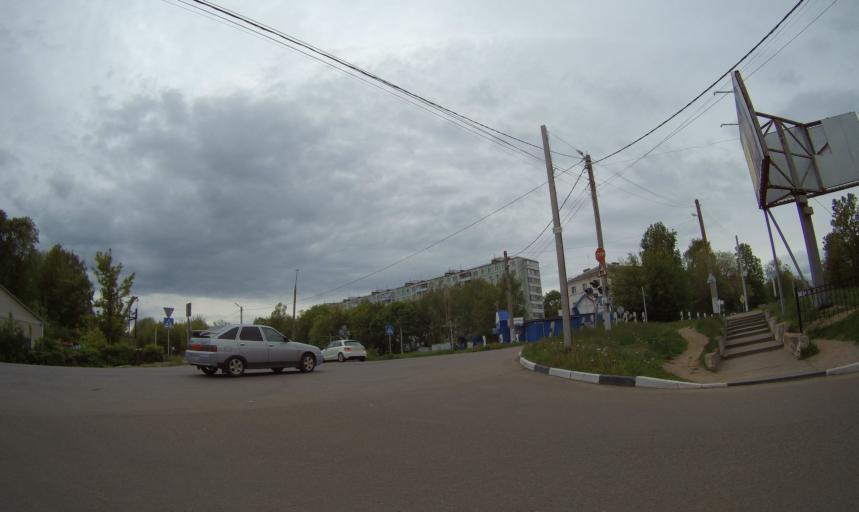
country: RU
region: Moskovskaya
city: Kolomna
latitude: 55.0744
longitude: 38.8015
